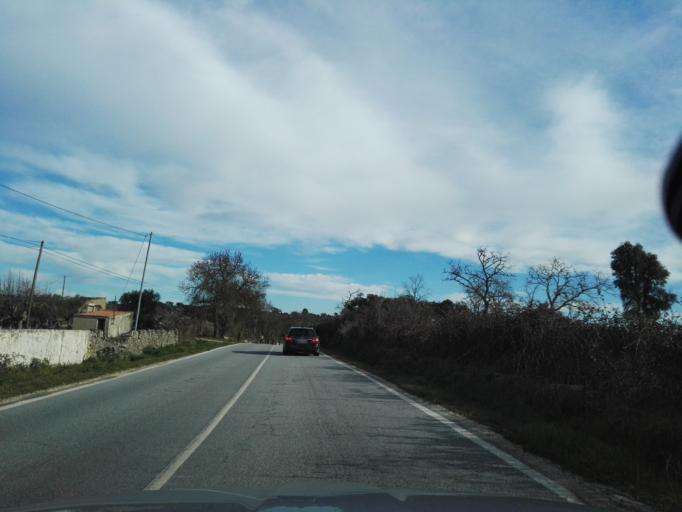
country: PT
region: Portalegre
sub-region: Nisa
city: Nisa
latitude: 39.5047
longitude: -7.6677
